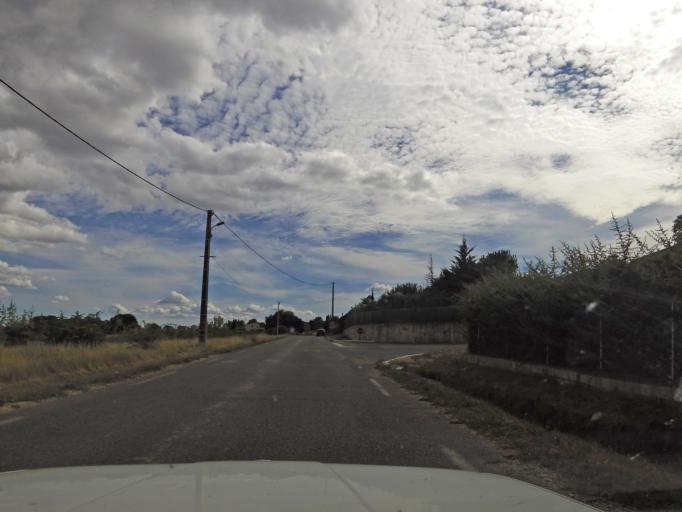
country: FR
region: Languedoc-Roussillon
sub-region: Departement du Gard
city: Bagard
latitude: 44.0824
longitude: 4.0584
